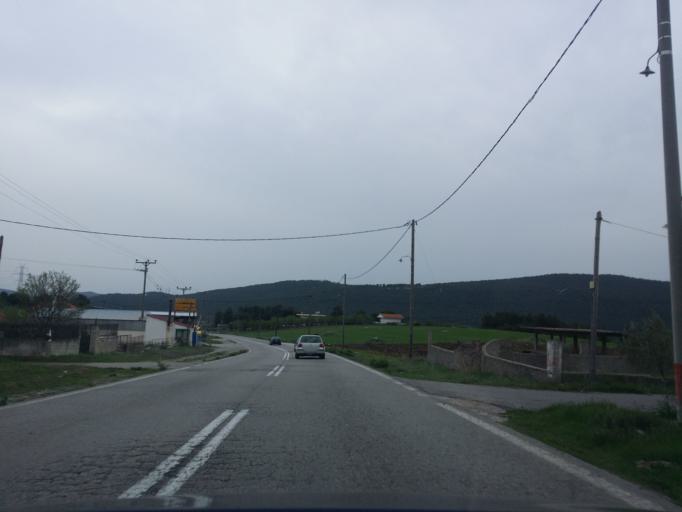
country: GR
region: Attica
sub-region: Nomarchia Dytikis Attikis
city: Vilia
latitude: 38.1736
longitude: 23.3852
